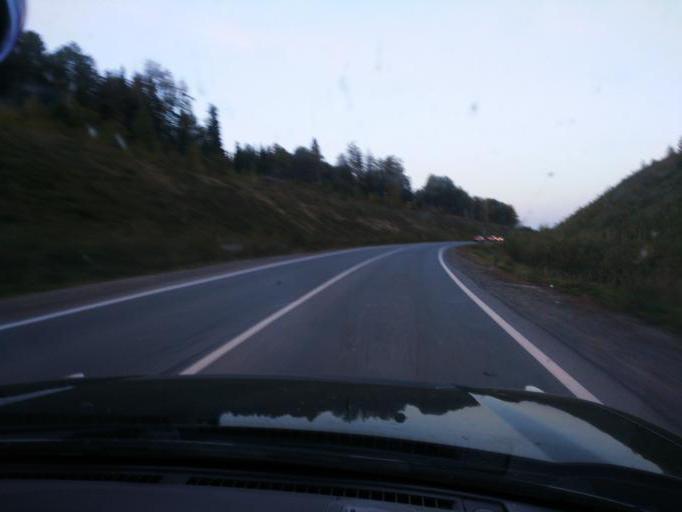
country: RU
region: Perm
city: Sylva
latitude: 58.2952
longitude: 56.8122
